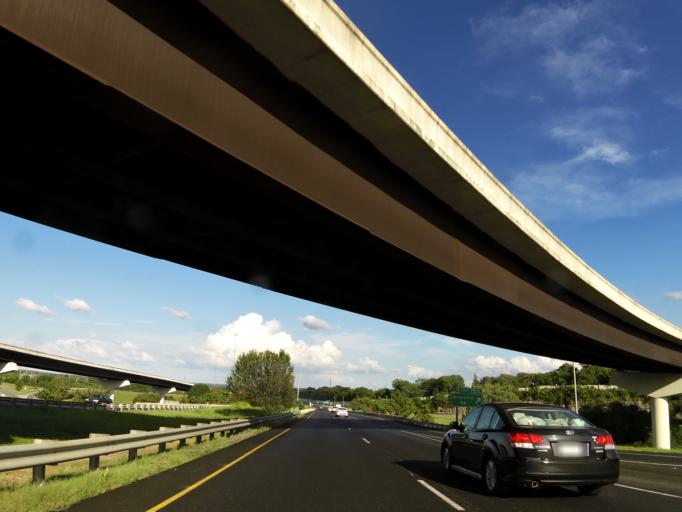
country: US
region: Tennessee
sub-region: Davidson County
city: Nashville
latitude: 36.2393
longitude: -86.7435
